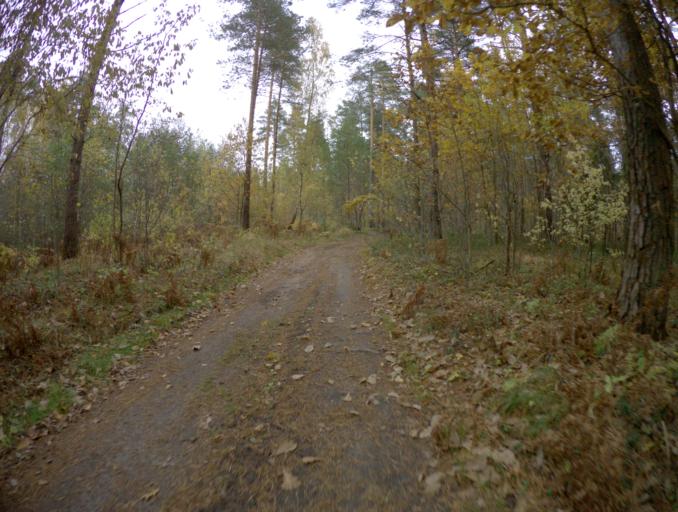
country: RU
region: Vladimir
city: Raduzhnyy
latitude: 56.0298
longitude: 40.4034
